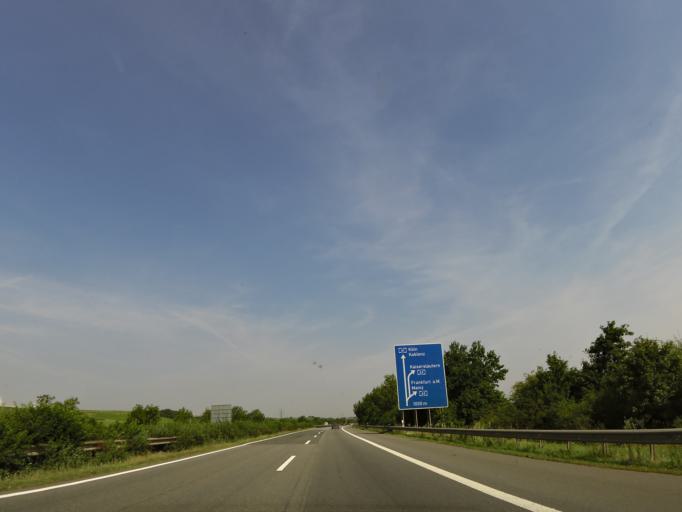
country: DE
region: Rheinland-Pfalz
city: Alzey
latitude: 49.7582
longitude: 8.1202
